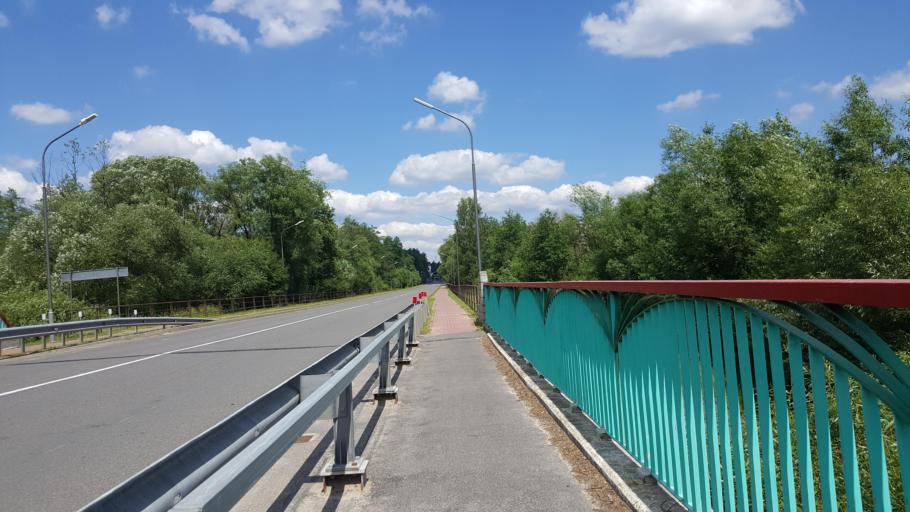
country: BY
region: Brest
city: Kamyanyuki
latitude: 52.5637
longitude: 23.8007
